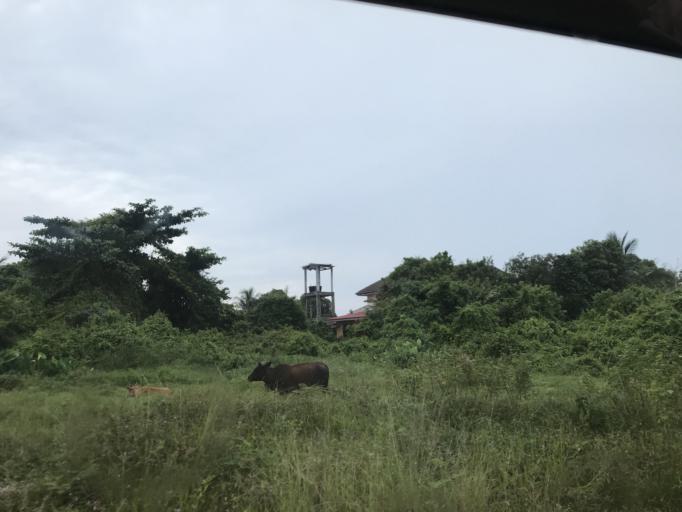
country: MY
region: Kelantan
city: Kota Bharu
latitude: 6.1178
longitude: 102.2068
